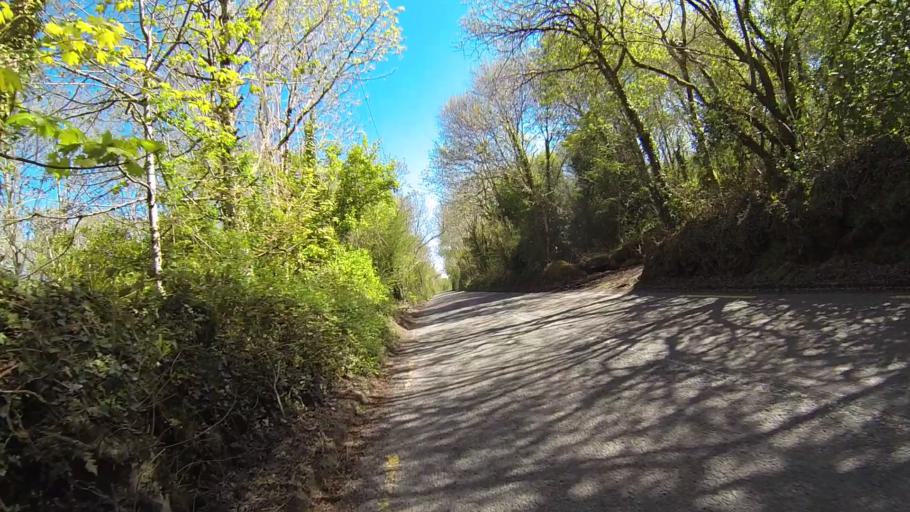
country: IE
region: Munster
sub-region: Ciarrai
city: Kenmare
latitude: 51.8548
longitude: -9.6264
